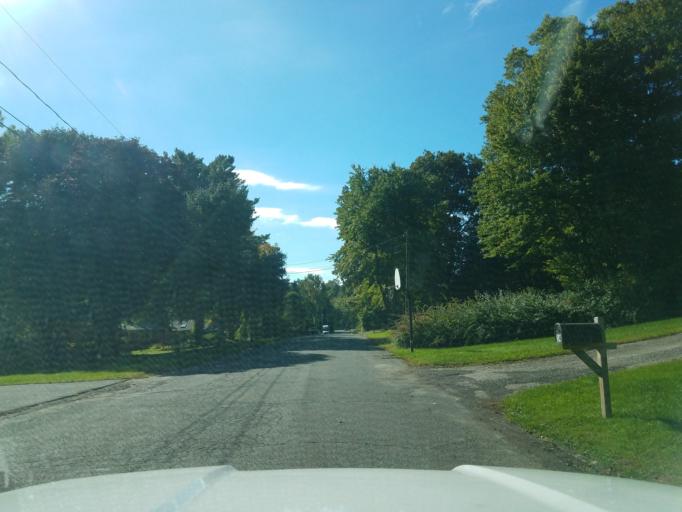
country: US
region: Connecticut
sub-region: Fairfield County
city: Trumbull
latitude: 41.3283
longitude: -73.2039
